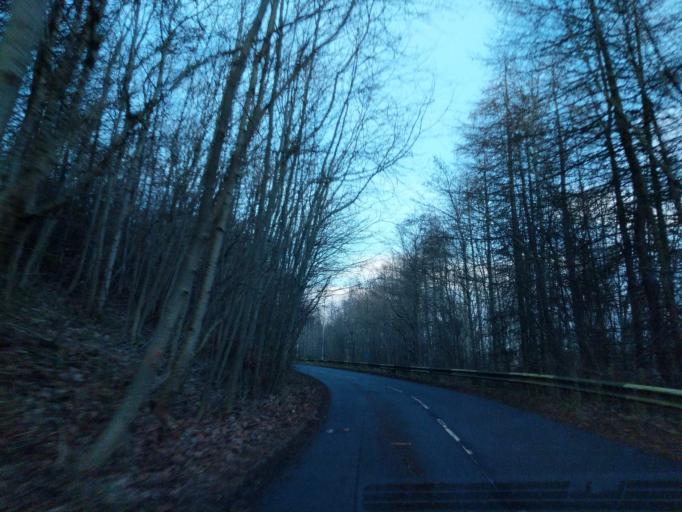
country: GB
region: Scotland
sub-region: Midlothian
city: Gorebridge
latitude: 55.8245
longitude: -3.0846
